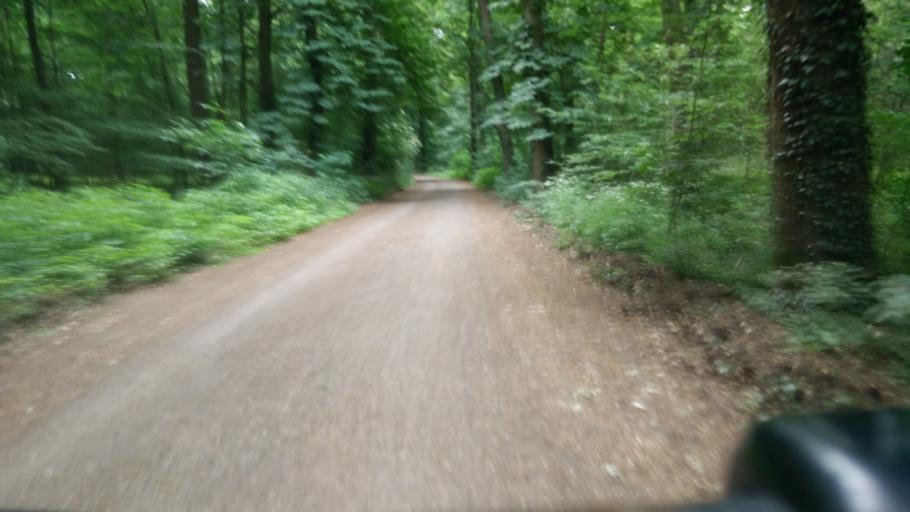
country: DE
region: Lower Saxony
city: Wunstorf
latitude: 52.4393
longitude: 9.3904
